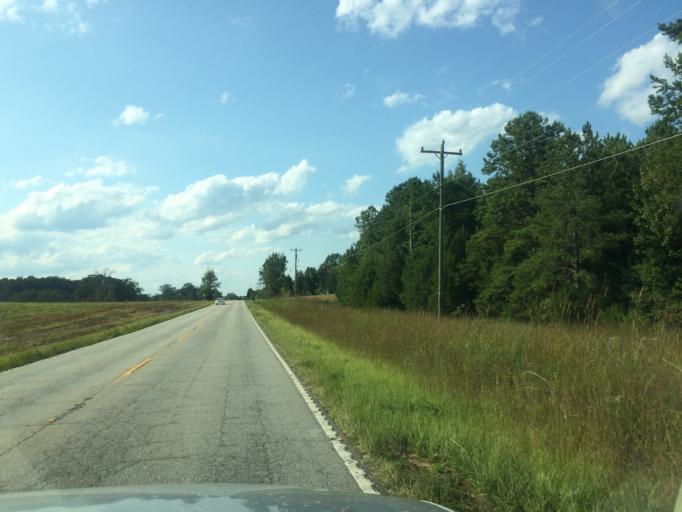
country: US
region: South Carolina
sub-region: Greenville County
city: Fountain Inn
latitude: 34.5524
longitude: -82.2078
